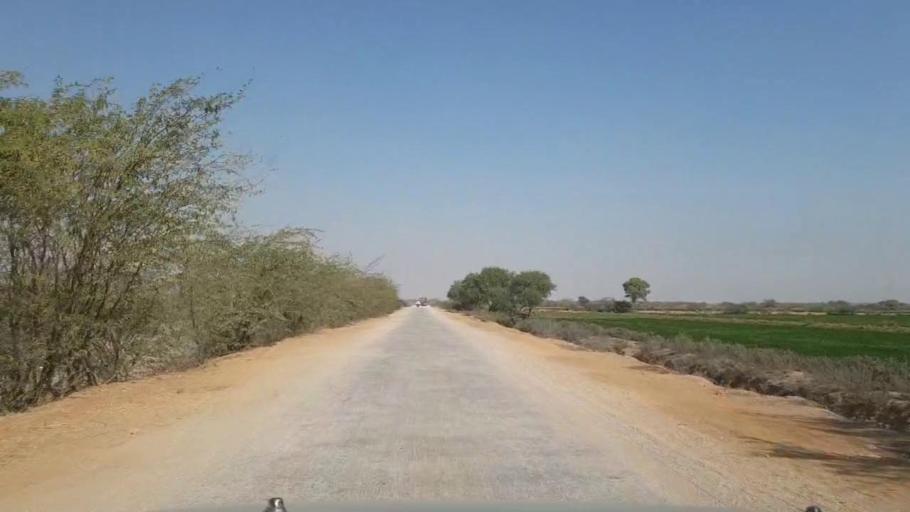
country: PK
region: Sindh
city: Thatta
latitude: 24.9583
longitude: 67.9583
